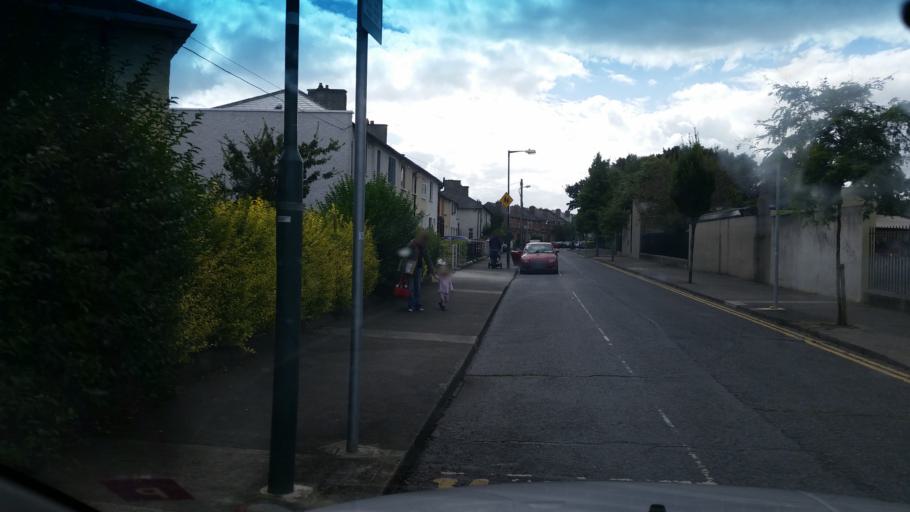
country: IE
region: Leinster
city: Rialto
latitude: 53.3346
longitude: -6.2786
